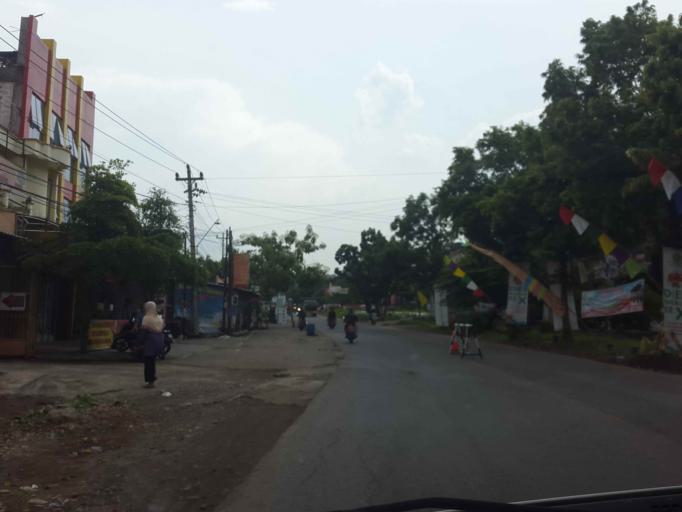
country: ID
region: Central Java
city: Semarang
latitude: -7.0309
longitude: 110.4587
